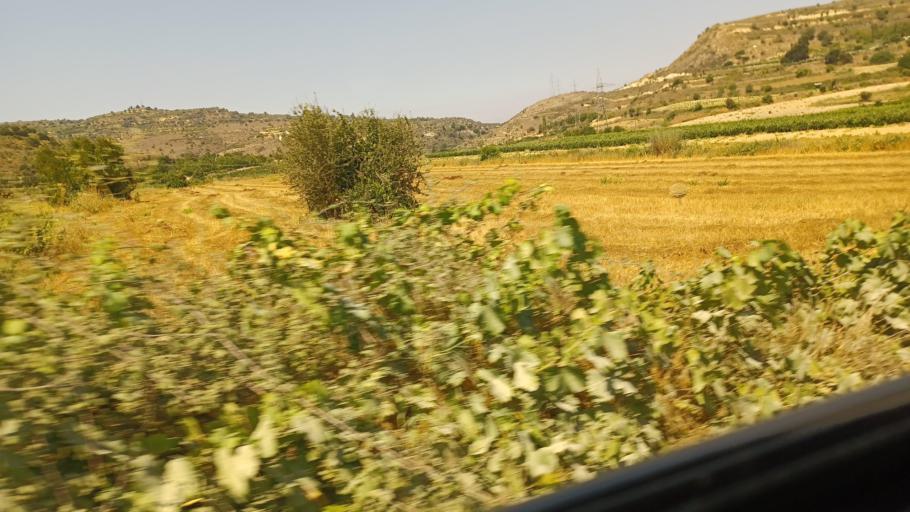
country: CY
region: Pafos
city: Mesogi
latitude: 34.8693
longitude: 32.4938
